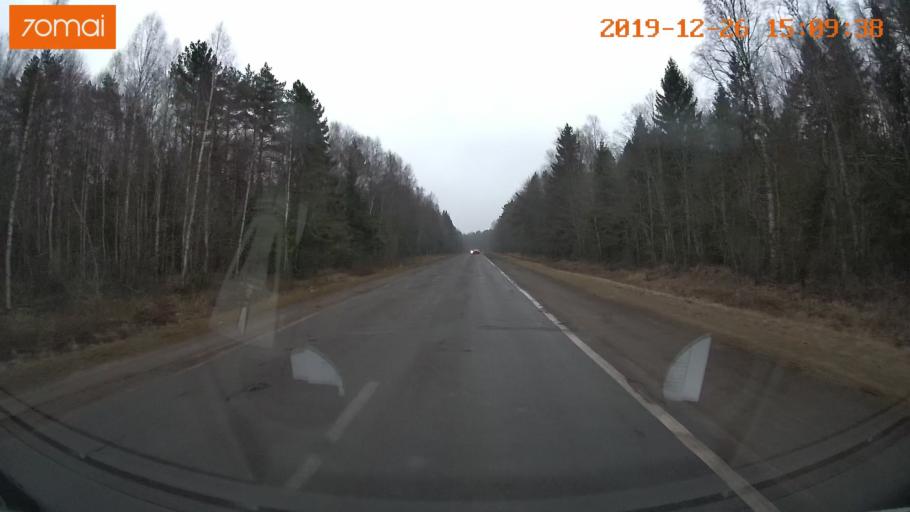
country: RU
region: Jaroslavl
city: Rybinsk
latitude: 58.1473
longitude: 38.8429
